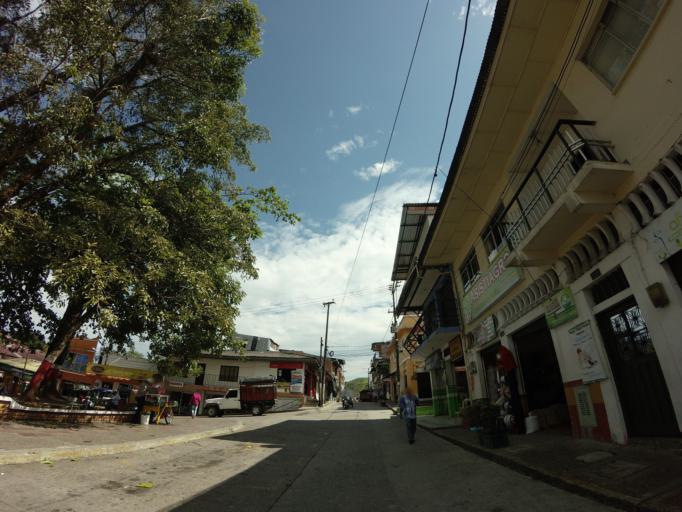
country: CO
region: Caldas
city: Norcasia
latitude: 5.5760
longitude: -74.8885
